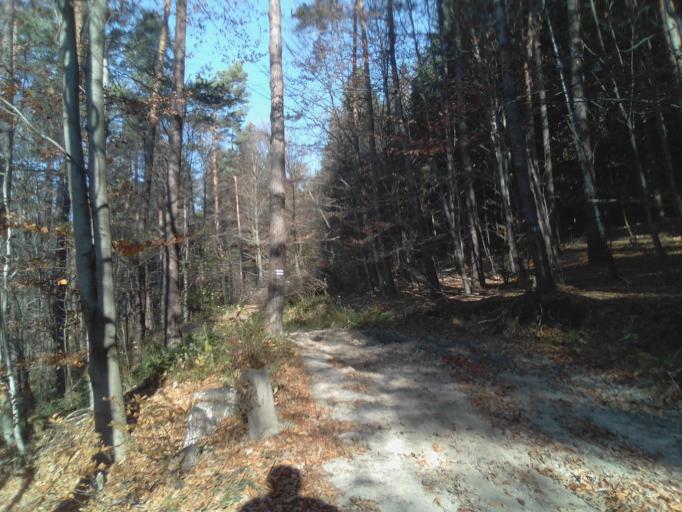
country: PL
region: Subcarpathian Voivodeship
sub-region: Powiat strzyzowski
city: Wysoka Strzyzowska
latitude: 49.8006
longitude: 21.7266
